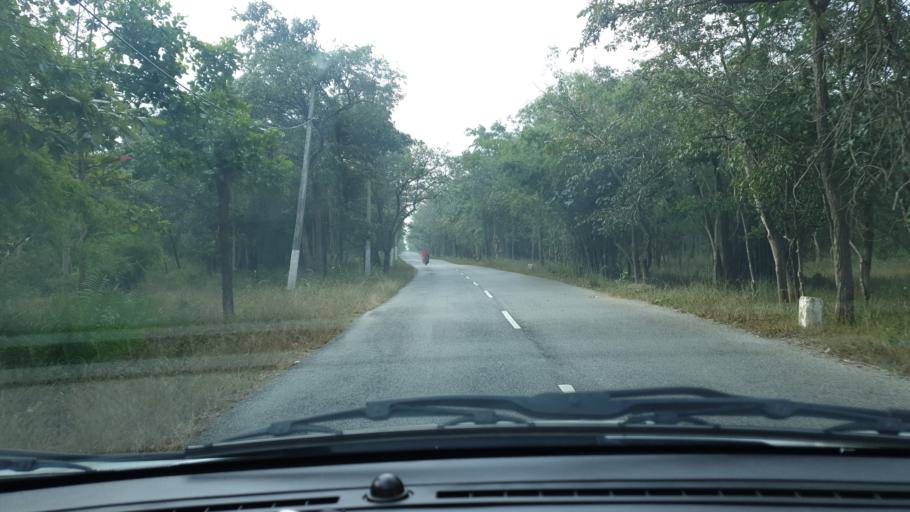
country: IN
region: Andhra Pradesh
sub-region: Kurnool
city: Srisailam
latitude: 16.3034
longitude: 78.7318
